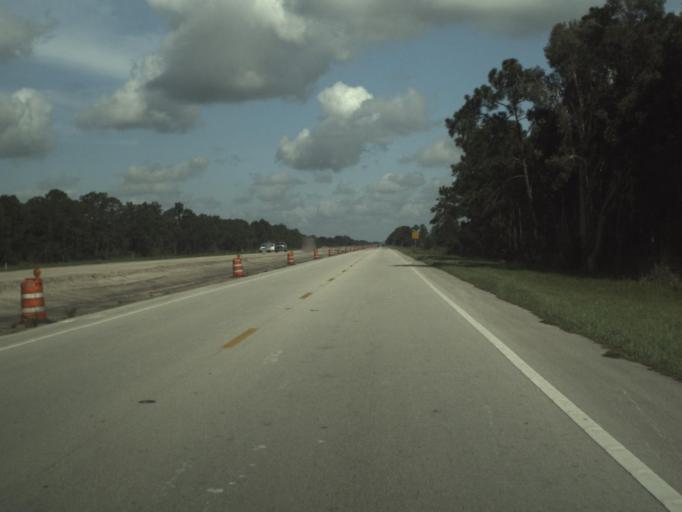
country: US
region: Florida
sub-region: Martin County
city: Indiantown
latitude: 26.9469
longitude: -80.3572
